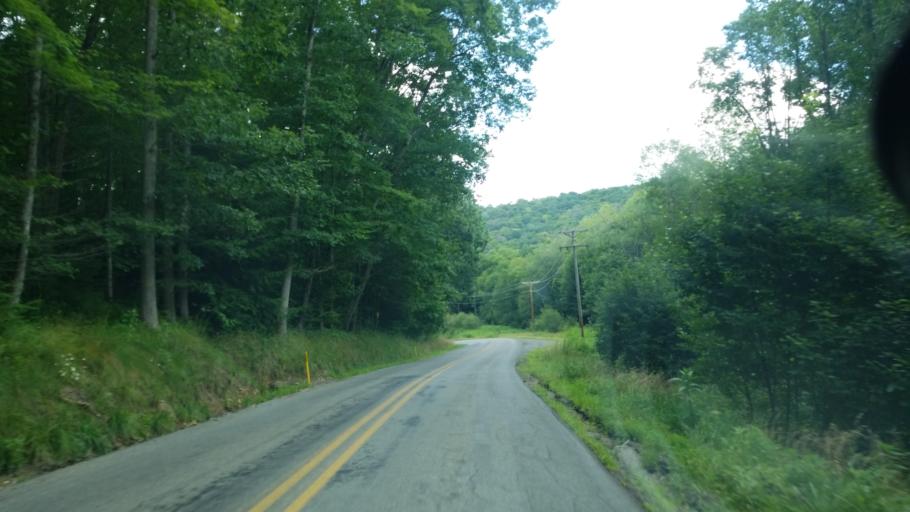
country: US
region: Pennsylvania
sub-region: Jefferson County
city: Brookville
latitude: 41.2273
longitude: -79.0522
